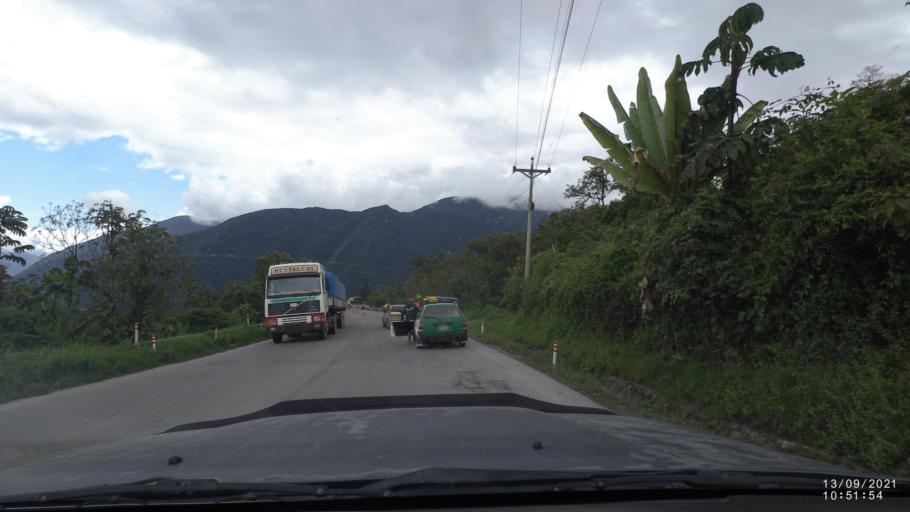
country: BO
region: Cochabamba
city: Colomi
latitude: -17.1988
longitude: -65.8397
